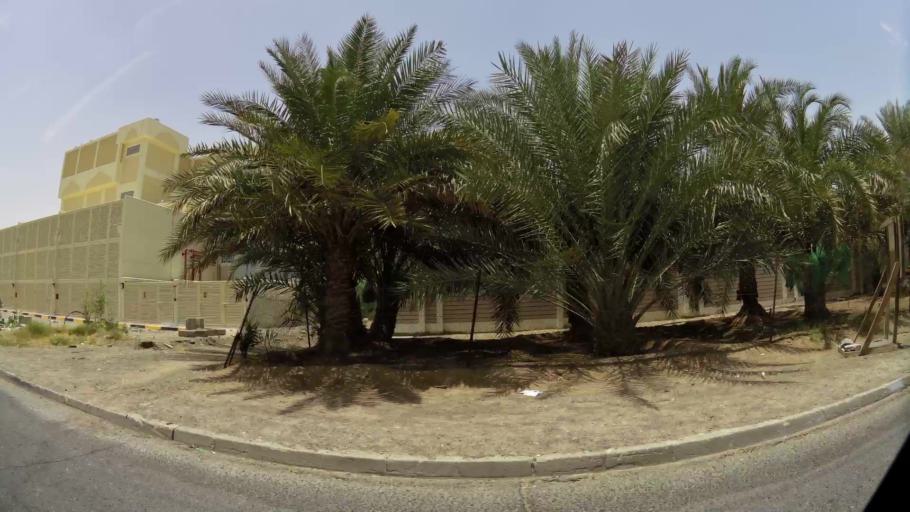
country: AE
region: Abu Dhabi
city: Al Ain
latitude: 24.2170
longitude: 55.7176
